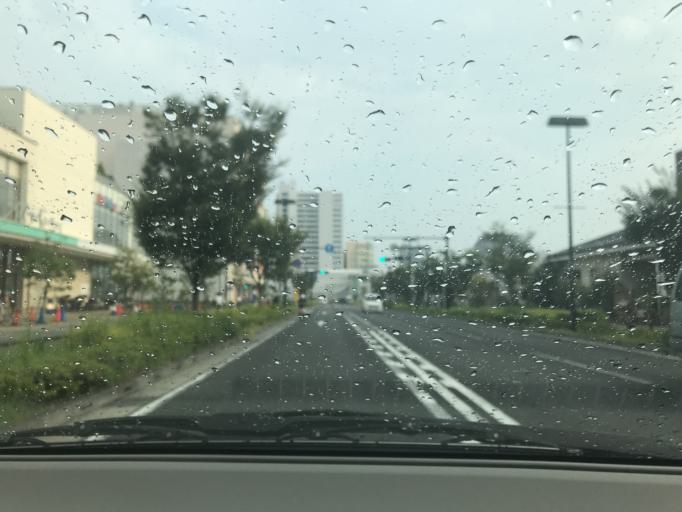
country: JP
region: Kanagawa
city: Fujisawa
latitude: 35.3394
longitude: 139.4474
